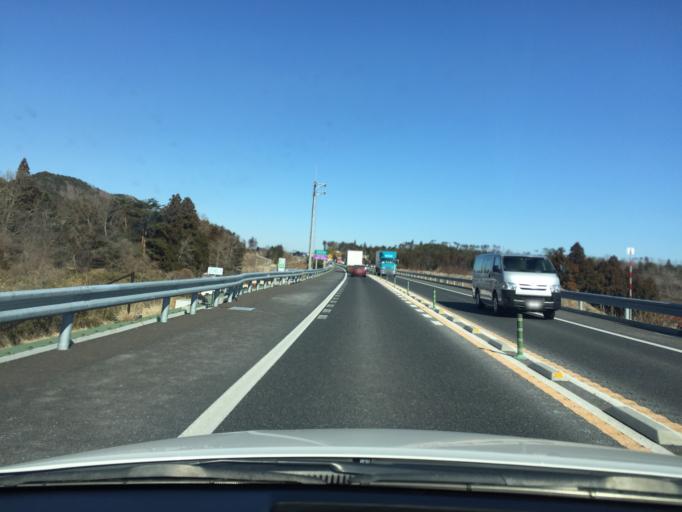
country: JP
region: Fukushima
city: Namie
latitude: 37.7059
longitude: 140.9231
